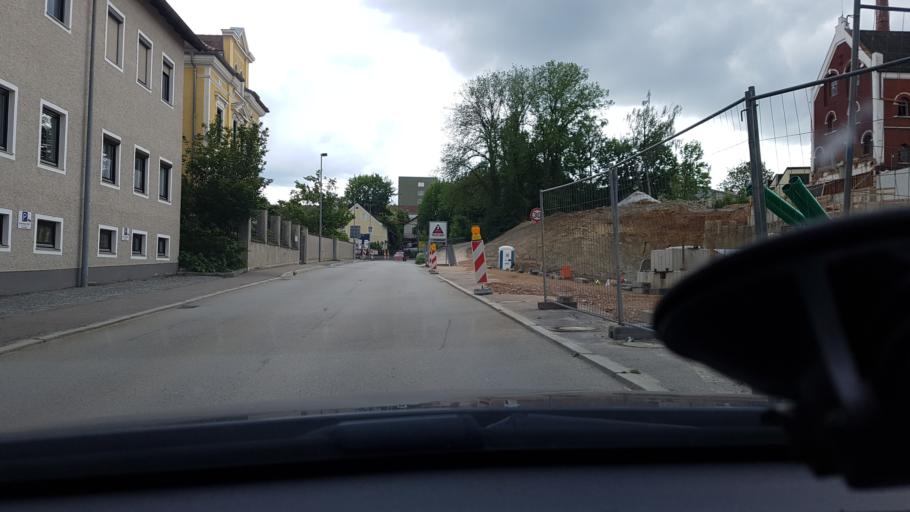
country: DE
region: Bavaria
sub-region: Lower Bavaria
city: Rotthalmunster
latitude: 48.3573
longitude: 13.2021
